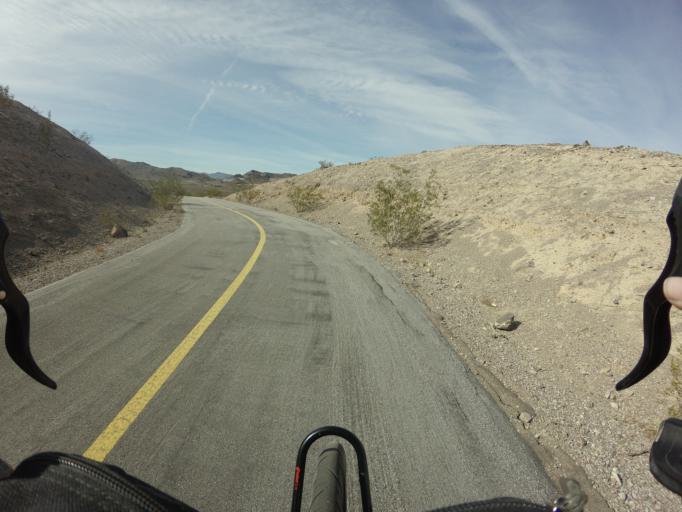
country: US
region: Nevada
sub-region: Clark County
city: Henderson
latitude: 36.1057
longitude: -114.8943
